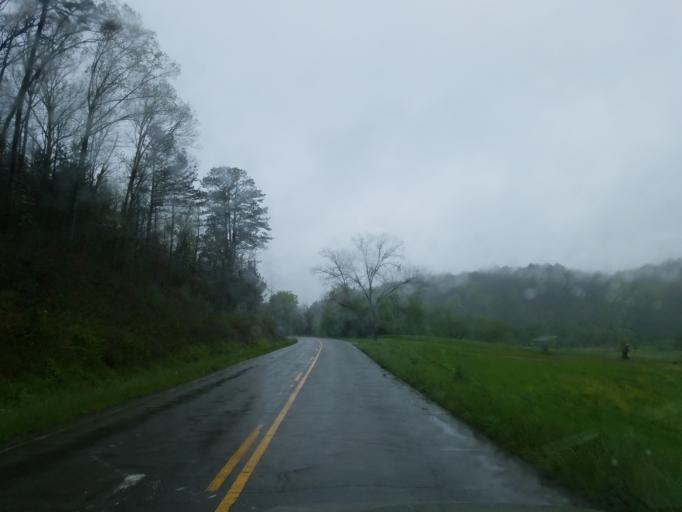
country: US
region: Georgia
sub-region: Gilmer County
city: Ellijay
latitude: 34.5861
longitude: -84.5335
